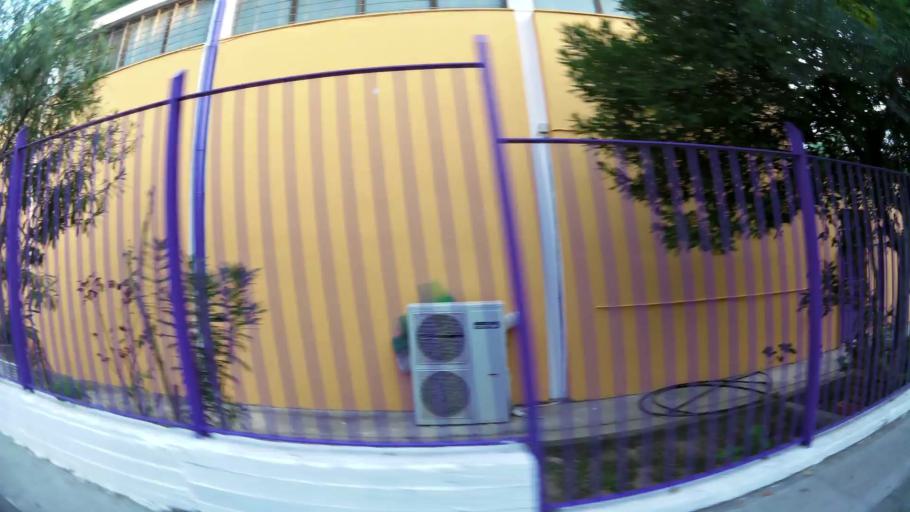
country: GR
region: Attica
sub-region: Nomarchia Athinas
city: Petroupolis
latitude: 38.0435
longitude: 23.6899
